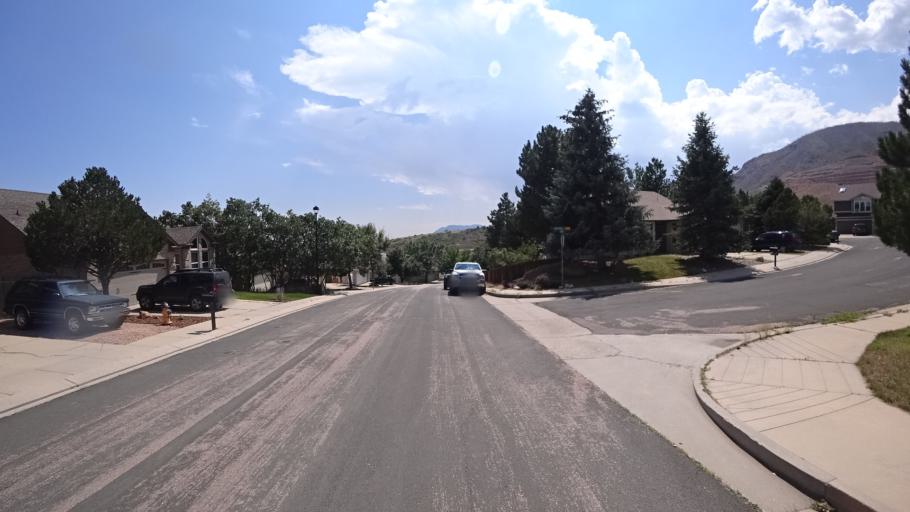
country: US
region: Colorado
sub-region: El Paso County
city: Air Force Academy
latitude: 38.9391
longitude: -104.8794
